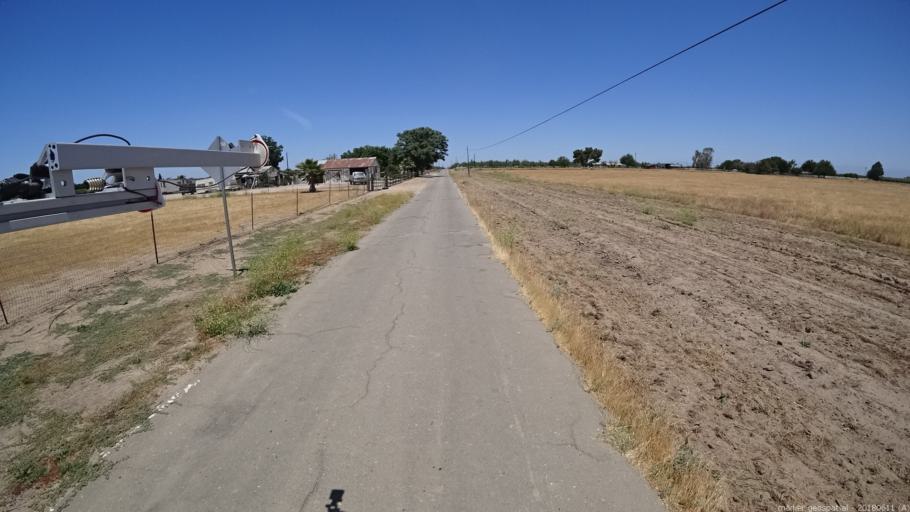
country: US
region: California
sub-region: Madera County
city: Fairmead
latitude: 37.0050
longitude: -120.1842
